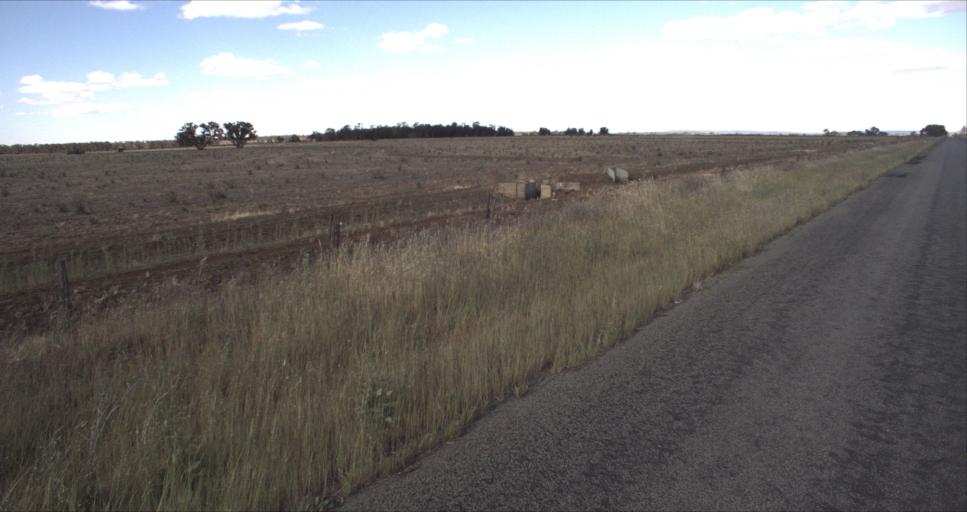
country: AU
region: New South Wales
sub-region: Leeton
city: Leeton
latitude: -34.4395
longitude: 146.2180
